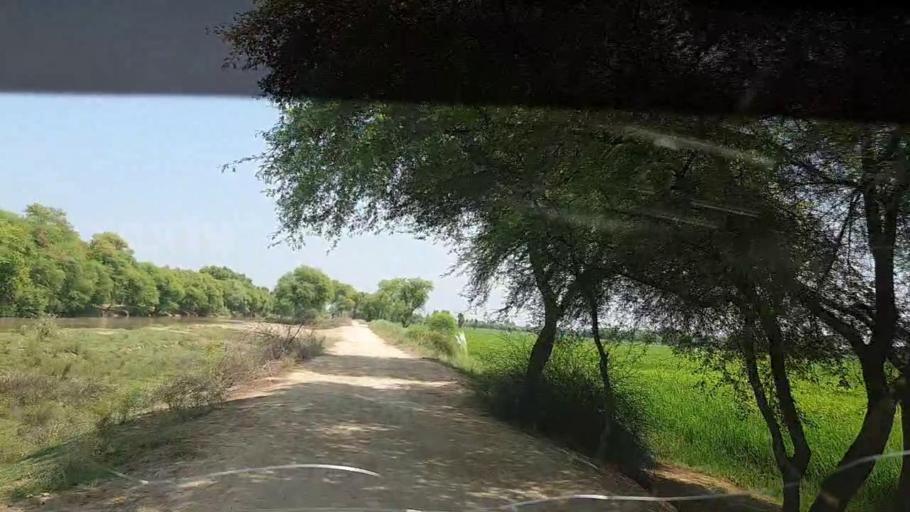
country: PK
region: Sindh
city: Tangwani
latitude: 28.2327
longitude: 68.9502
